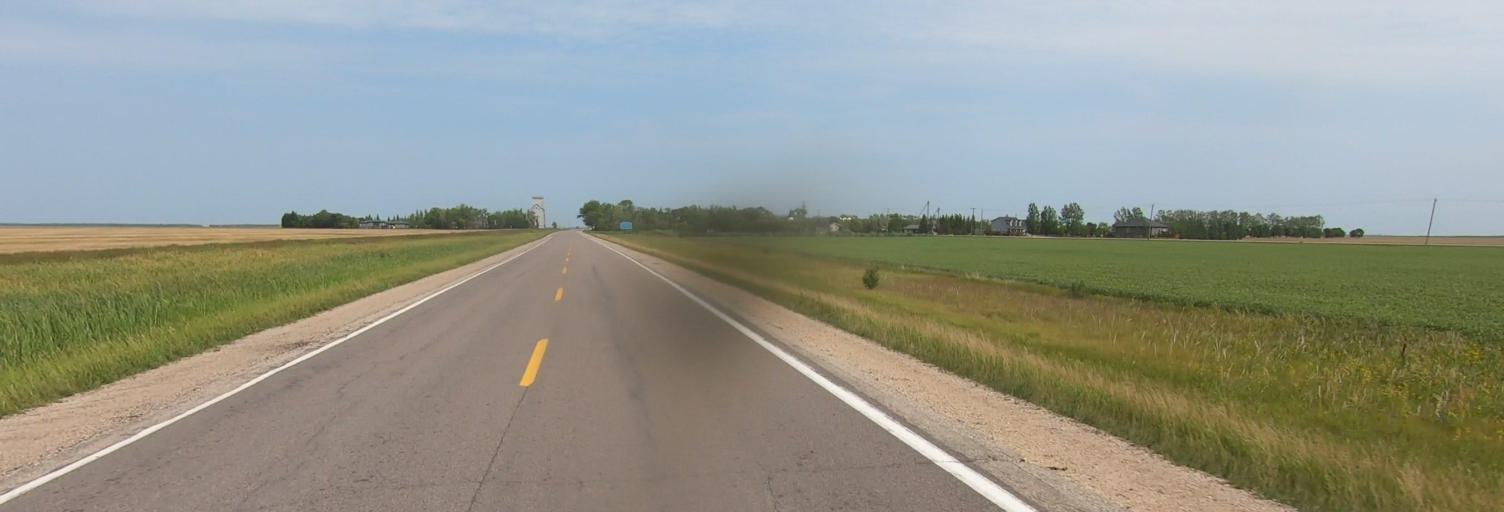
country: CA
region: Manitoba
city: Morris
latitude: 49.6075
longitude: -97.3259
